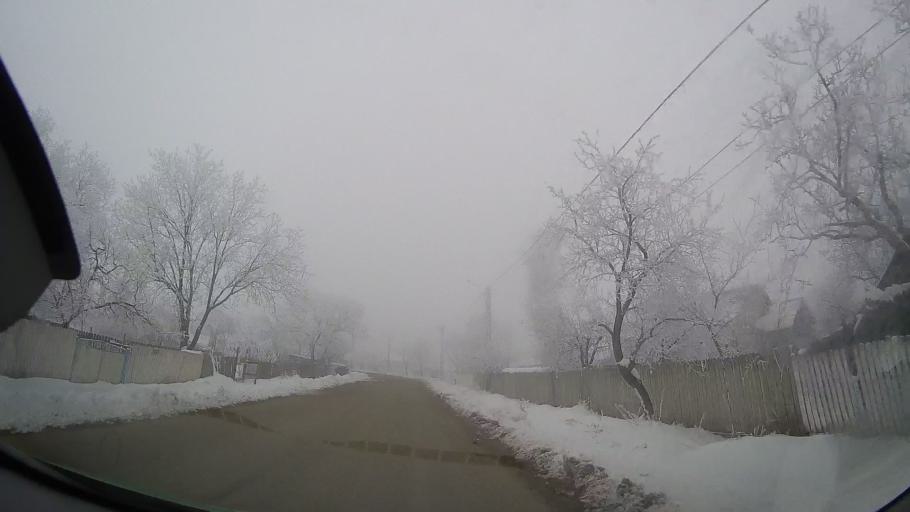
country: RO
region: Iasi
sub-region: Comuna Tansa
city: Suhulet
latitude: 46.8970
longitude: 27.2653
